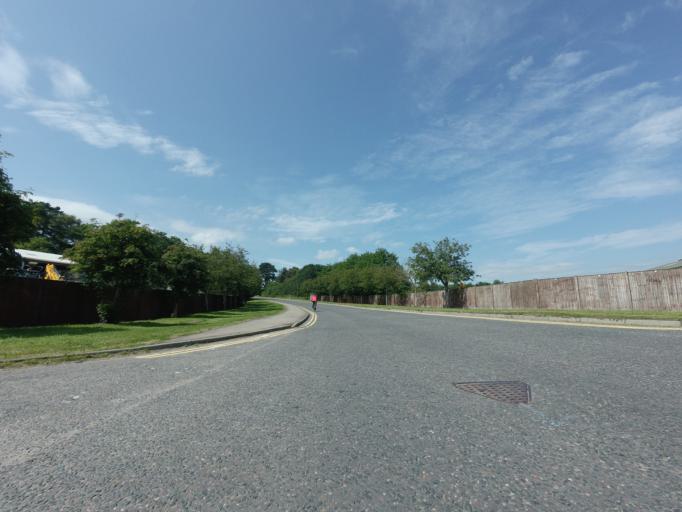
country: GB
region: Scotland
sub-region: Highland
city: Tain
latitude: 57.8176
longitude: -4.0615
